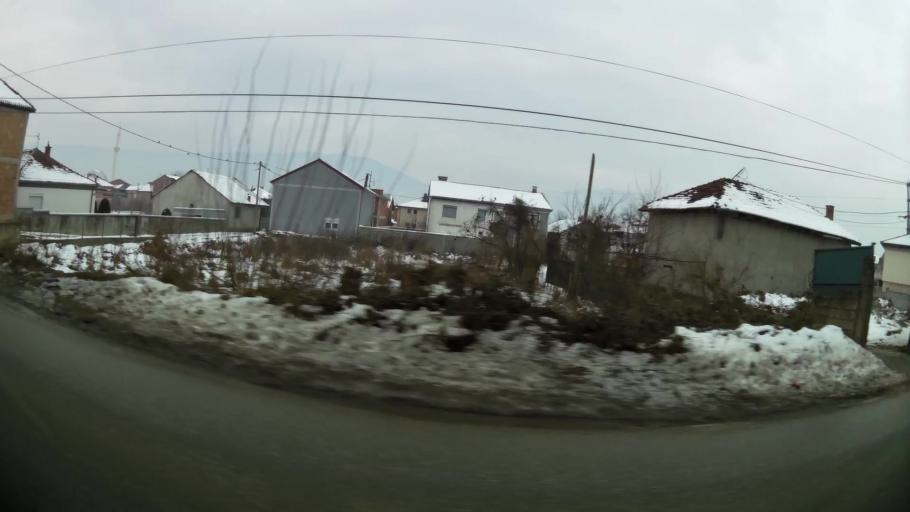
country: MK
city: Kondovo
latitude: 42.0111
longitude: 21.3172
